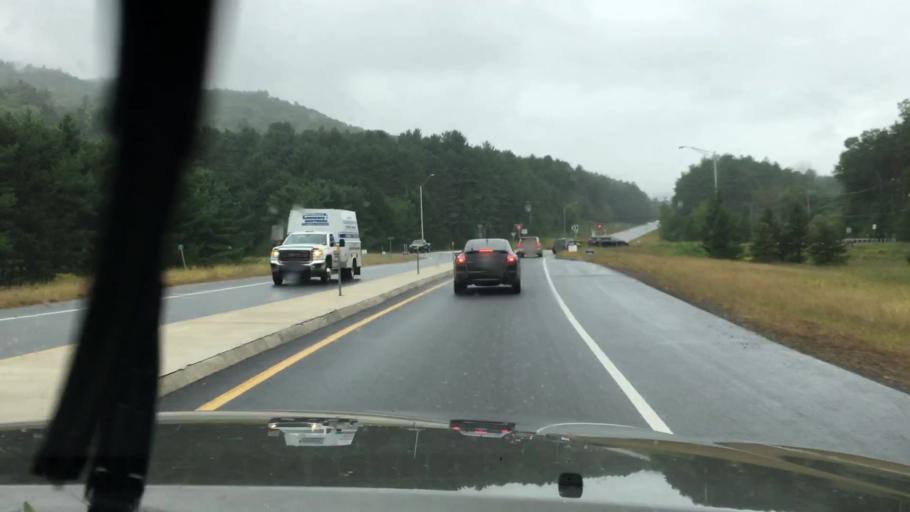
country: US
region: New Hampshire
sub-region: Cheshire County
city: Keene
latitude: 42.9243
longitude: -72.3111
